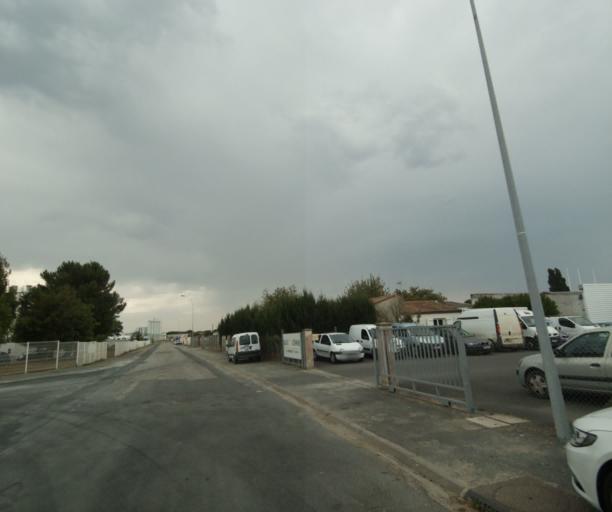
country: FR
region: Poitou-Charentes
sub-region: Departement de la Charente-Maritime
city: Tonnay-Charente
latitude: 45.9521
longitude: -0.8905
